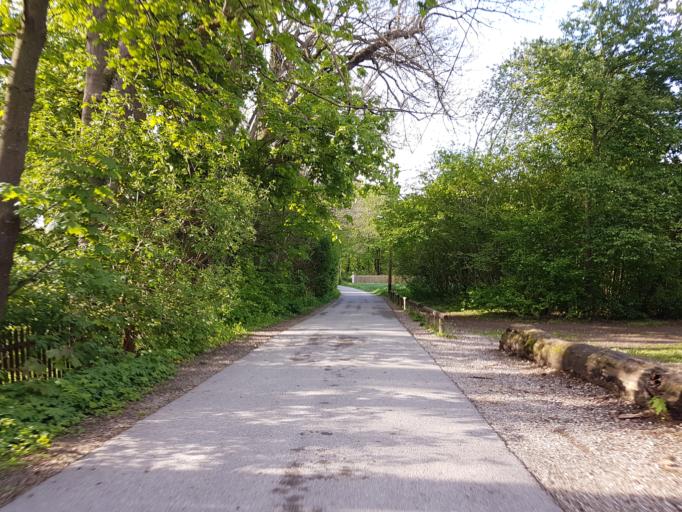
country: DE
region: Bavaria
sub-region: Upper Bavaria
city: Karlsfeld
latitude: 48.1797
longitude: 11.4597
